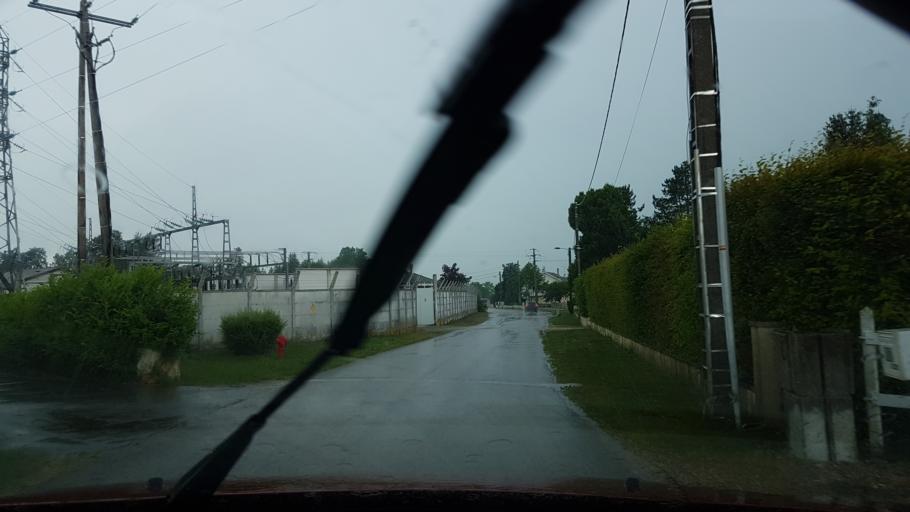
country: FR
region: Franche-Comte
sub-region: Departement du Jura
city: Clairvaux-les-Lacs
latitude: 46.5793
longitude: 5.6936
